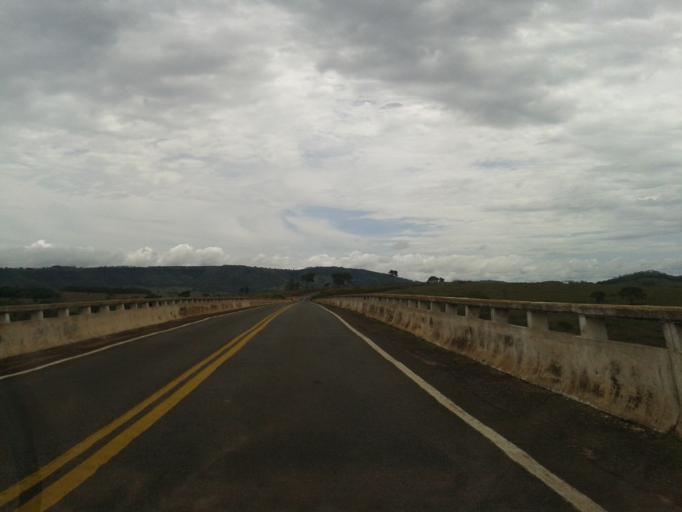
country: BR
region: Goias
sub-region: Buriti Alegre
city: Buriti Alegre
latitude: -18.1466
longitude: -48.8594
